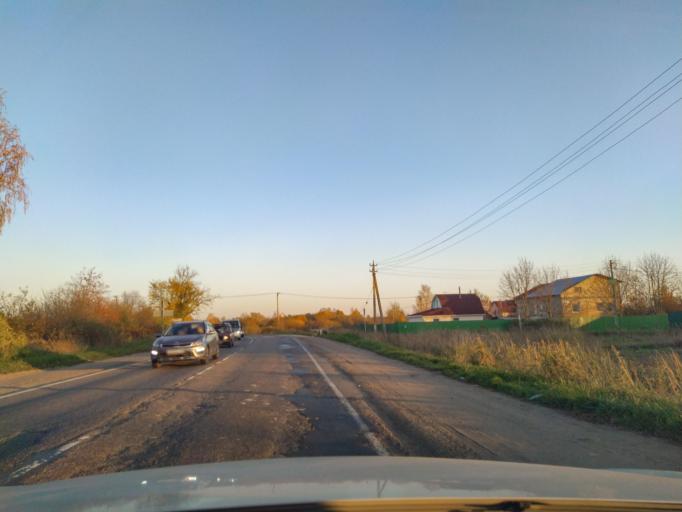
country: RU
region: Leningrad
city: Maloye Verevo
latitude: 59.6169
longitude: 30.2108
